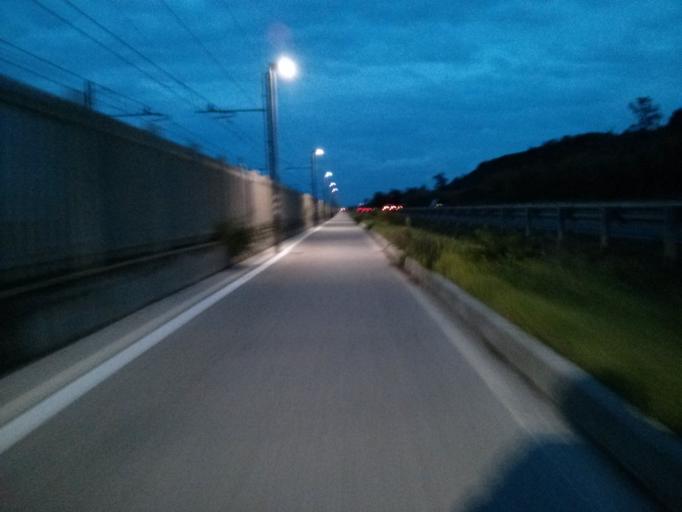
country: IT
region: The Marches
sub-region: Provincia di Pesaro e Urbino
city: Fenile
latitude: 43.8725
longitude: 12.9748
